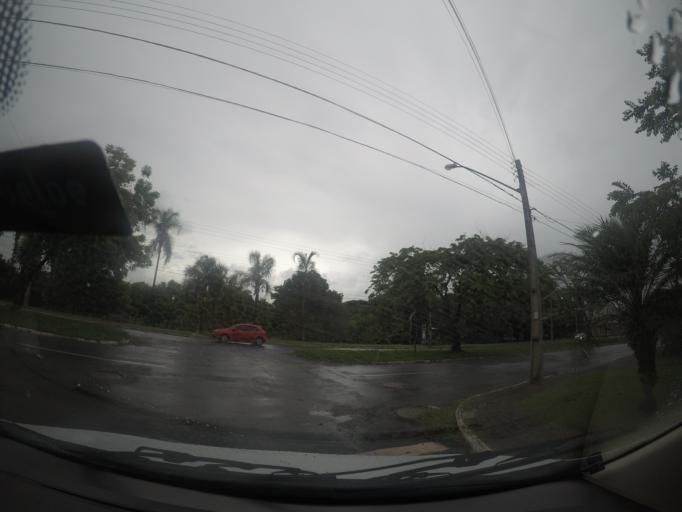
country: BR
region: Goias
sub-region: Goiania
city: Goiania
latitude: -16.6511
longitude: -49.2318
